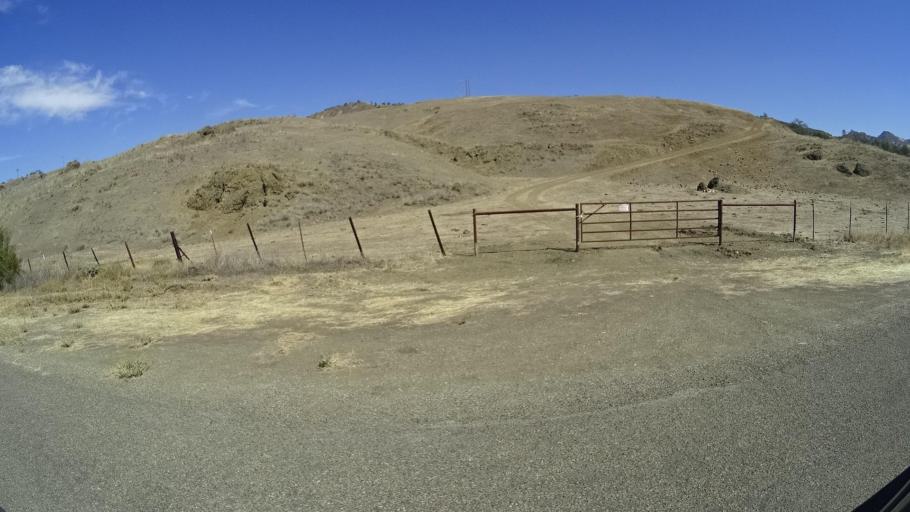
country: US
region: California
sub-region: Fresno County
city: Coalinga
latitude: 36.0975
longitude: -120.6850
